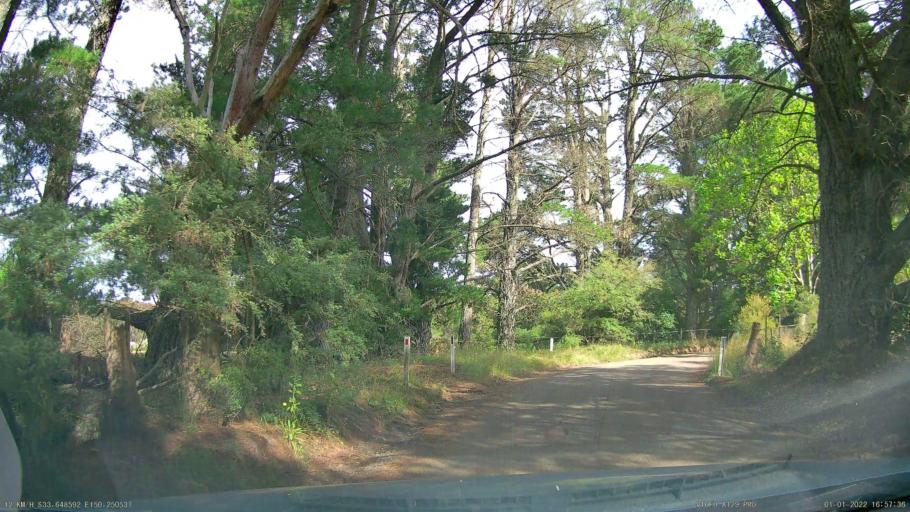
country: AU
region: New South Wales
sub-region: Blue Mountains Municipality
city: Blackheath
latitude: -33.6487
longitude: 150.2506
